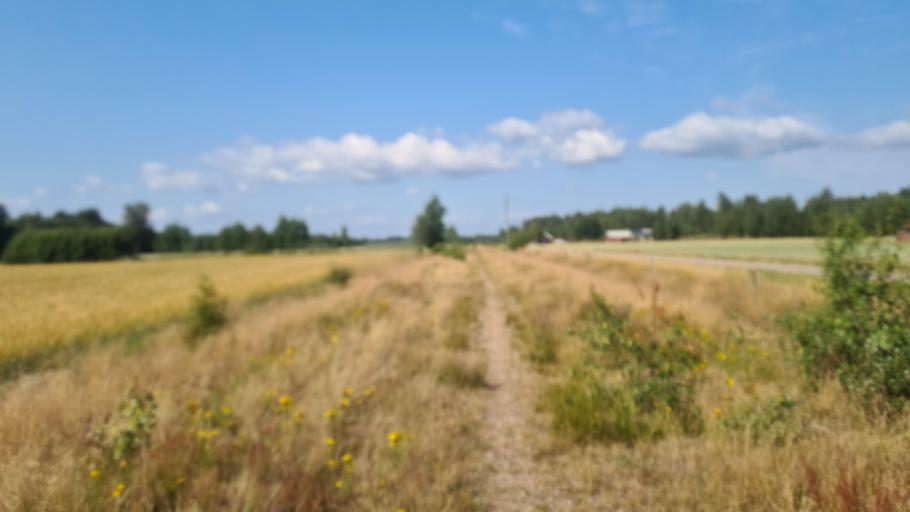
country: SE
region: Kronoberg
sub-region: Ljungby Kommun
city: Ljungby
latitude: 56.7494
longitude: 13.8820
